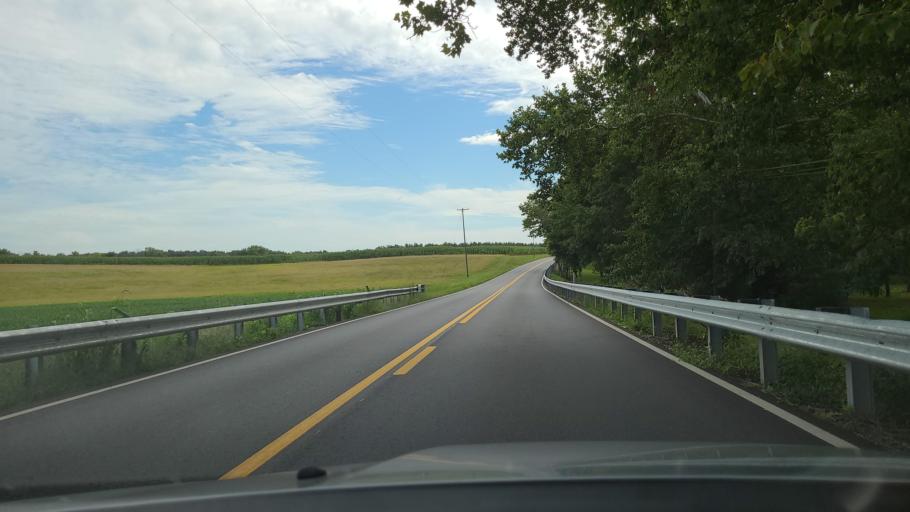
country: US
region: Maryland
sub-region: Frederick County
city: Thurmont
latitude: 39.6135
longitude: -77.3584
